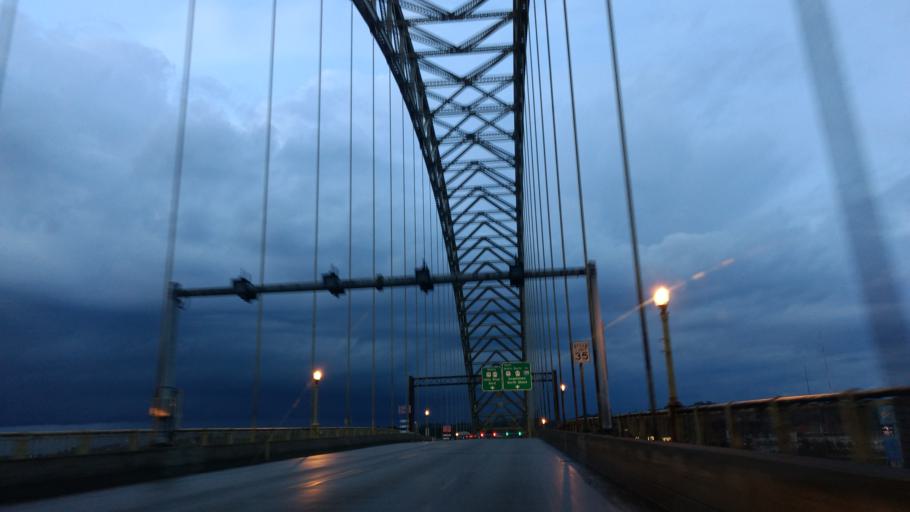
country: US
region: Pennsylvania
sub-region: Allegheny County
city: Pittsburgh
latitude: 40.4459
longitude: -80.0272
